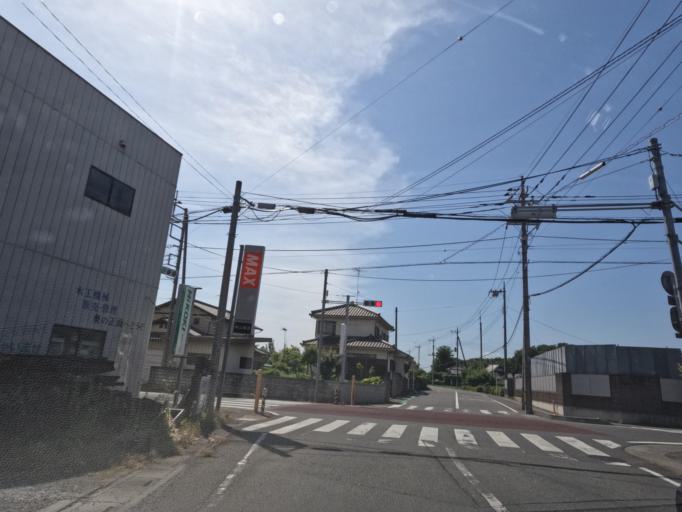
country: JP
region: Saitama
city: Kumagaya
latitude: 36.1065
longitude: 139.3256
